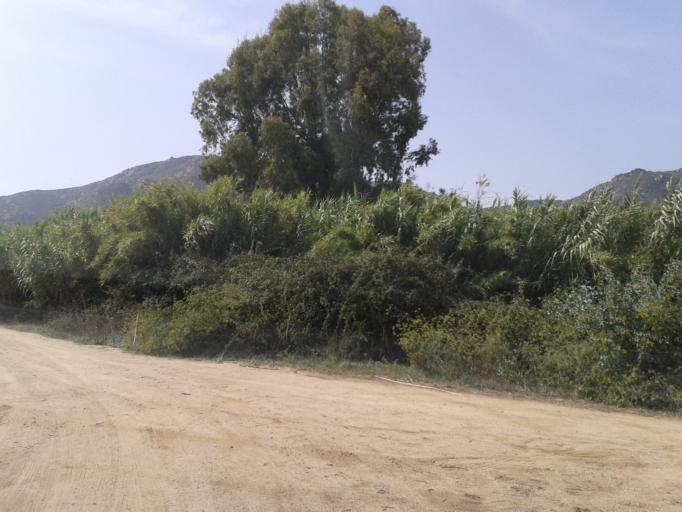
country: IT
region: Sardinia
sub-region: Provincia di Cagliari
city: Villasimius
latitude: 39.1385
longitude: 9.4967
